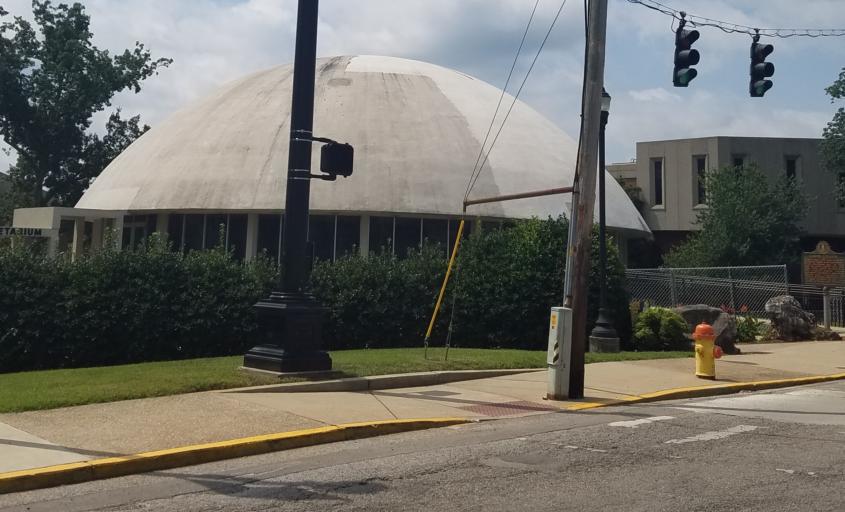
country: US
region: Kentucky
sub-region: Warren County
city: Bowling Green
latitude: 36.9869
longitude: -86.4495
